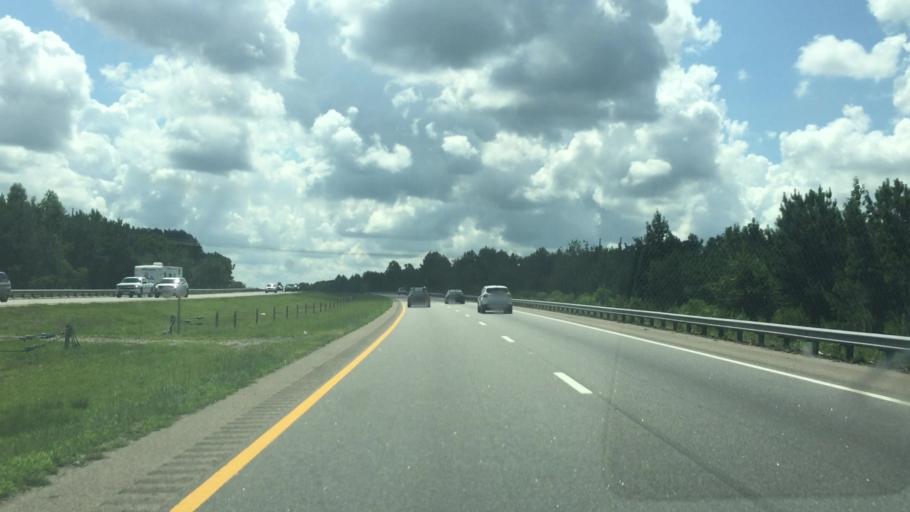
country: US
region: North Carolina
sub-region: Richmond County
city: East Rockingham
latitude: 34.8850
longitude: -79.7861
